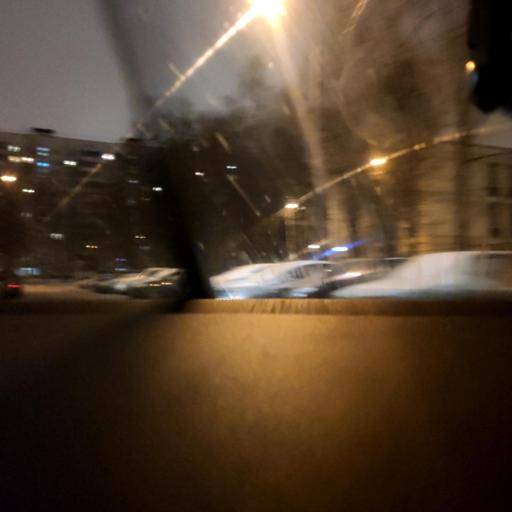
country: RU
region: Moscow
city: Ivanovskoye
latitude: 55.7703
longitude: 37.8303
